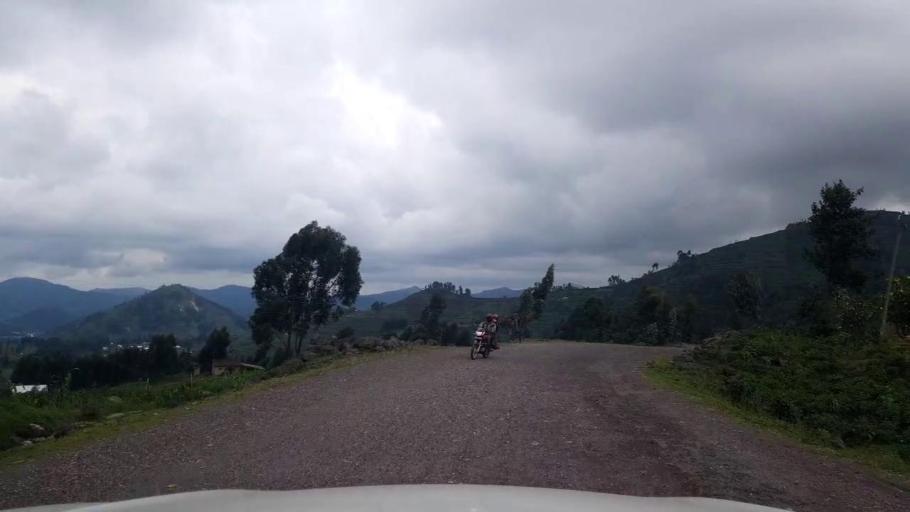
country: RW
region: Northern Province
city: Musanze
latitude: -1.5857
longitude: 29.4728
